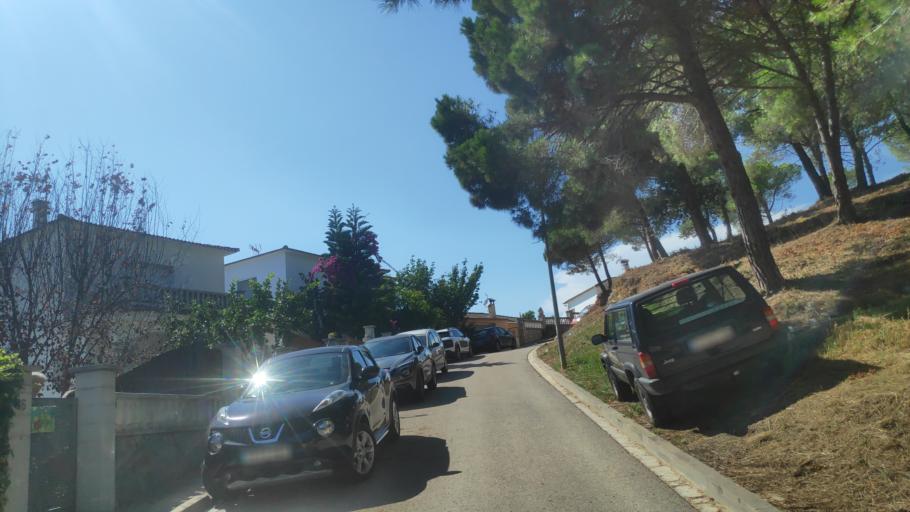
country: ES
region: Catalonia
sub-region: Provincia de Girona
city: Lloret de Mar
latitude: 41.7267
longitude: 2.8284
